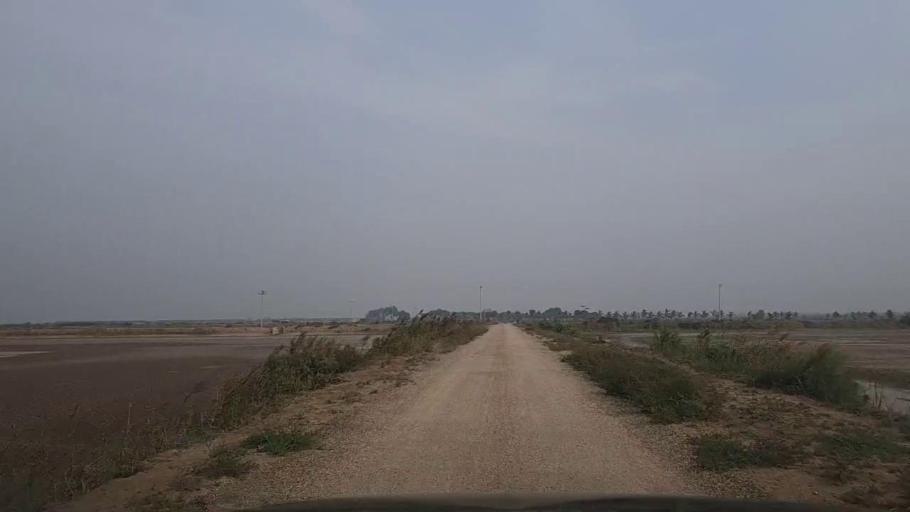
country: PK
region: Sindh
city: Chuhar Jamali
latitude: 24.5029
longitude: 67.8796
